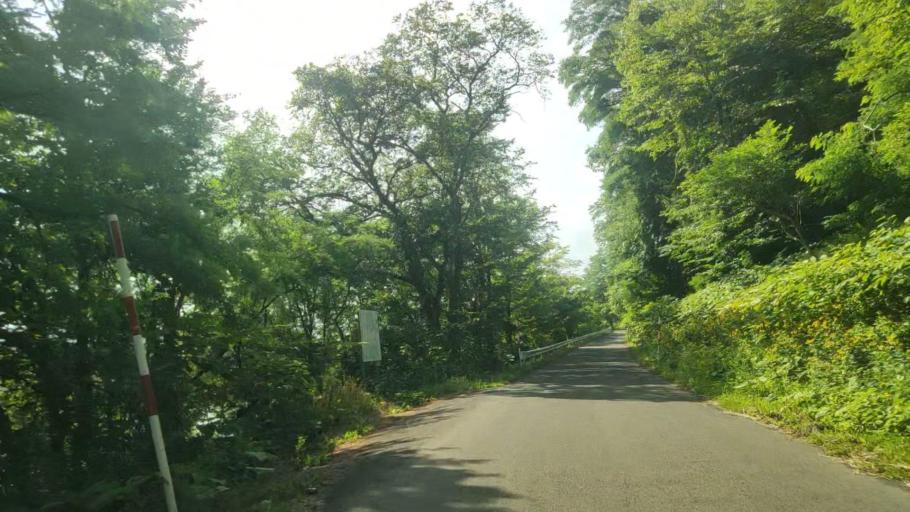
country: JP
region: Hokkaido
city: Shimo-furano
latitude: 43.3434
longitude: 142.3736
